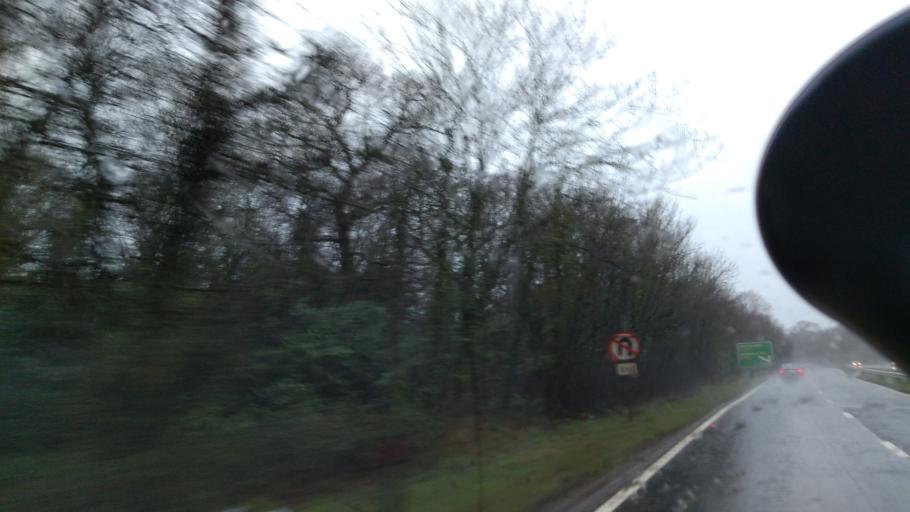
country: GB
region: England
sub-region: West Sussex
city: Goring-by-Sea
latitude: 50.8402
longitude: -0.4338
